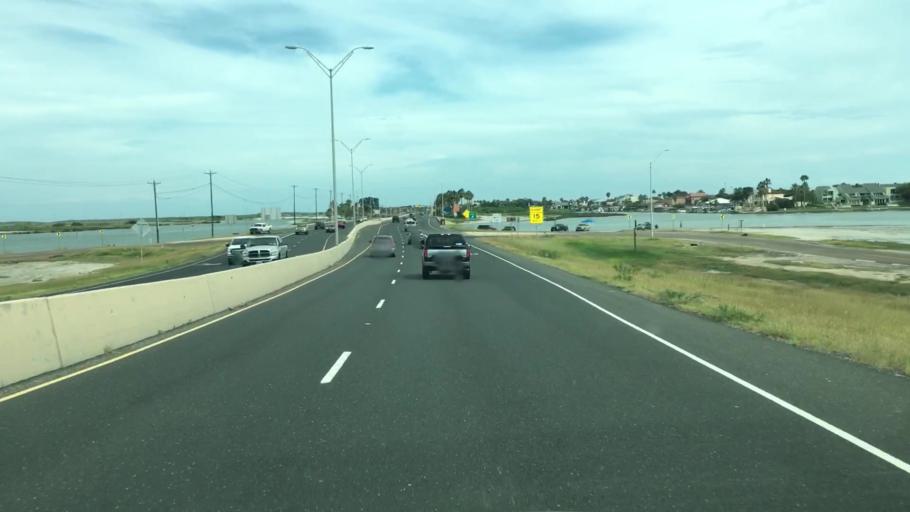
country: US
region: Texas
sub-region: Nueces County
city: Corpus Christi
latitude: 27.6327
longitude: -97.2351
